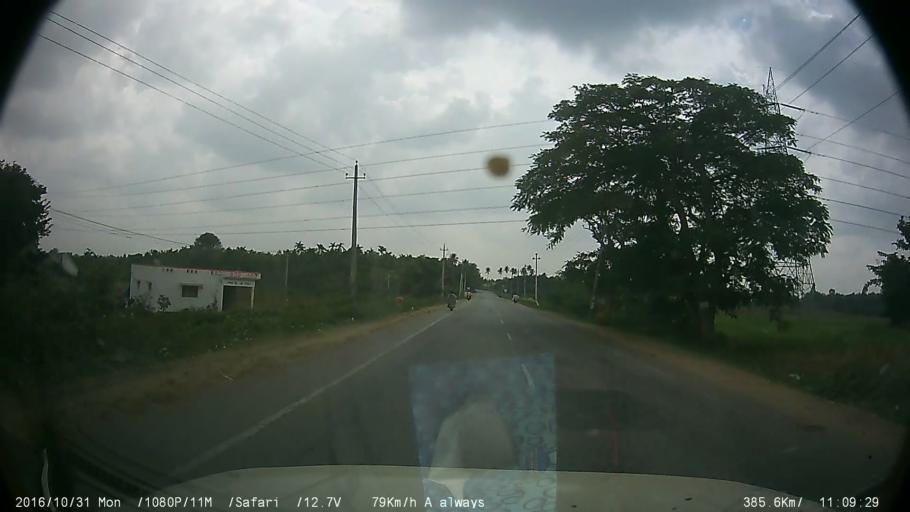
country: IN
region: Karnataka
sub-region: Mysore
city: Piriyapatna
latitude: 12.3531
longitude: 76.0677
